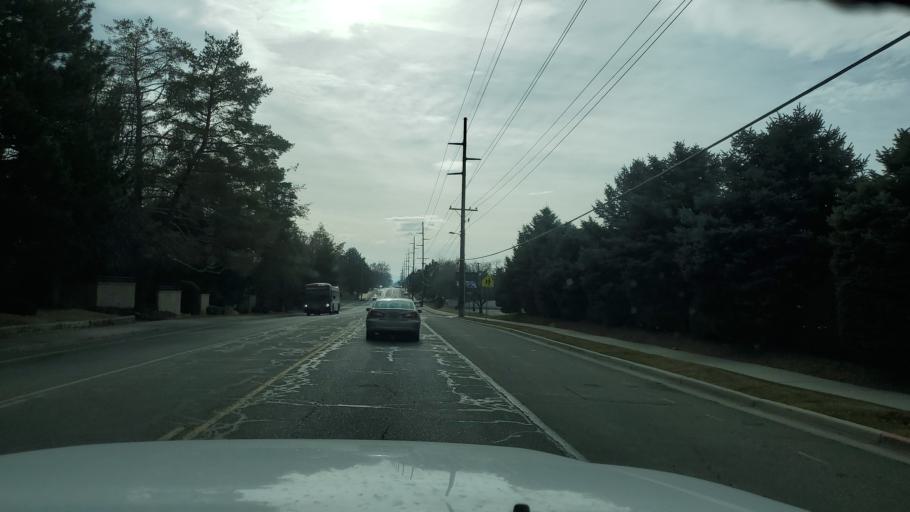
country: US
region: Utah
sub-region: Salt Lake County
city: Millcreek
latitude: 40.6854
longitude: -111.8656
